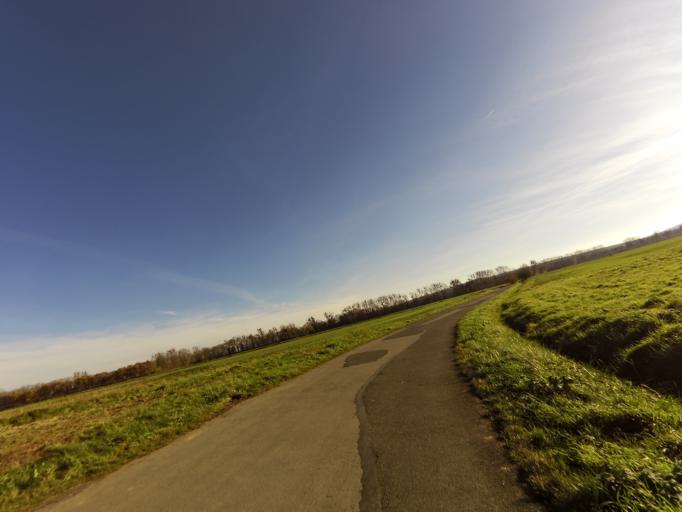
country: DE
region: North Rhine-Westphalia
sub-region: Regierungsbezirk Koln
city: Euskirchen
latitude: 50.6361
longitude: 6.8664
